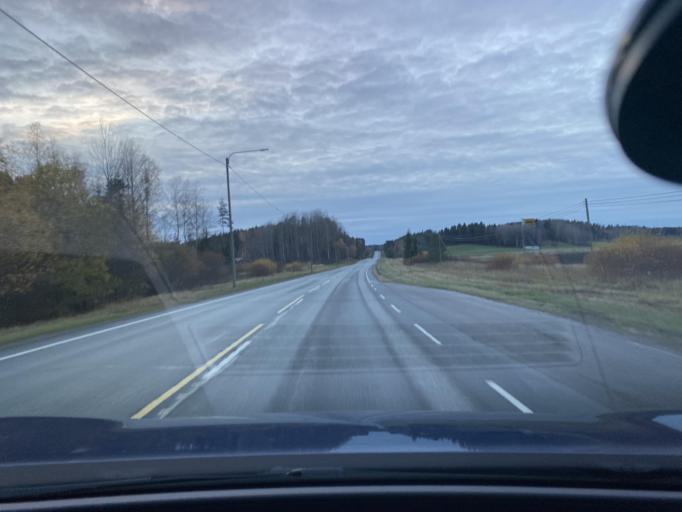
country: FI
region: Uusimaa
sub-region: Helsinki
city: Saukkola
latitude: 60.3855
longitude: 24.0665
